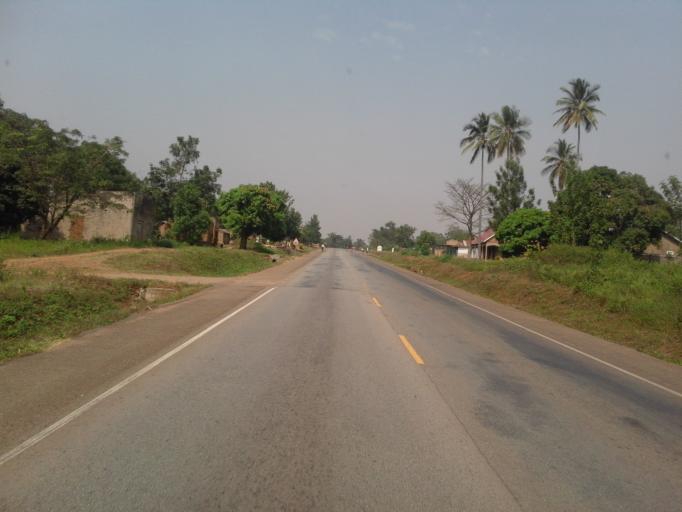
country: UG
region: Eastern Region
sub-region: Bugiri District
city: Bugiri
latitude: 0.6212
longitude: 33.6337
